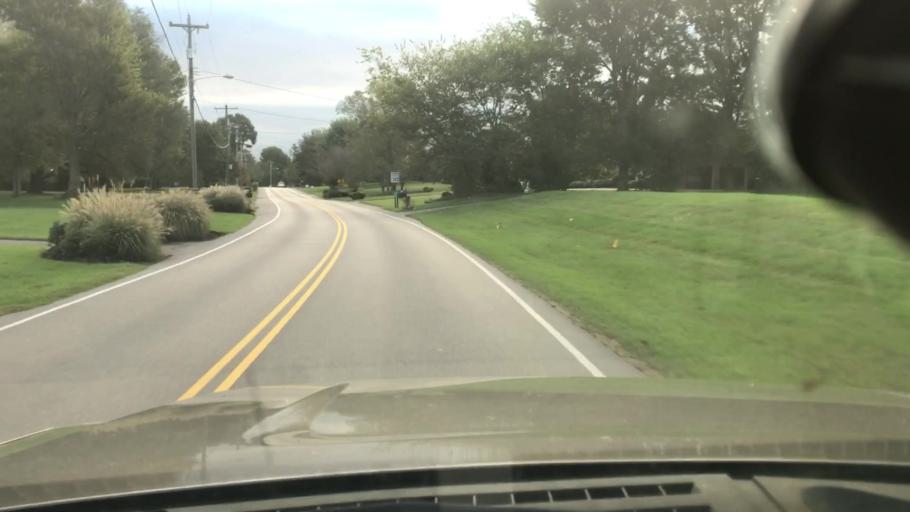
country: US
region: Tennessee
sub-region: Davidson County
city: Forest Hills
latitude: 36.0261
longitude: -86.8277
